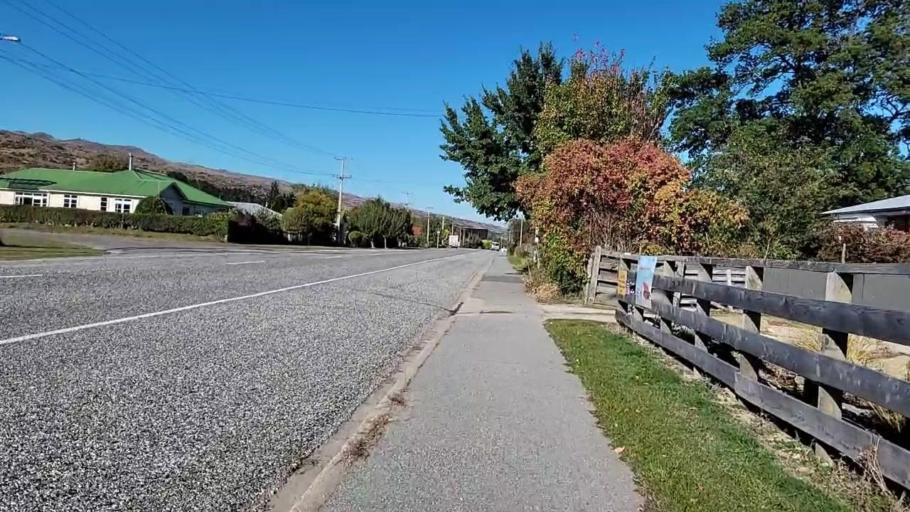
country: NZ
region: Otago
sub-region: Queenstown-Lakes District
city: Wanaka
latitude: -45.0053
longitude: 169.9146
